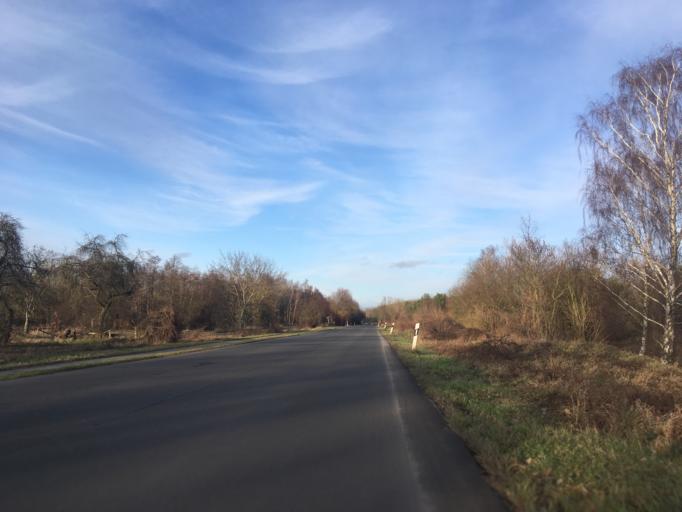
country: DE
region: Berlin
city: Blankenfelde
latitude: 52.6241
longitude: 13.3993
